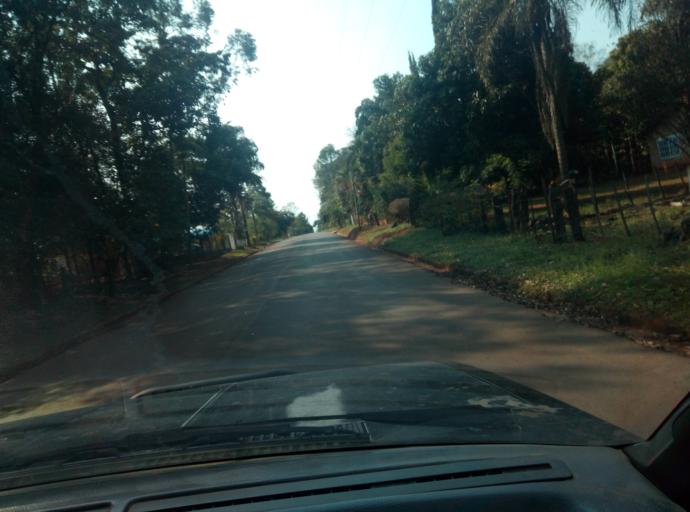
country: PY
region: Caaguazu
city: Carayao
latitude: -25.2106
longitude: -56.2953
